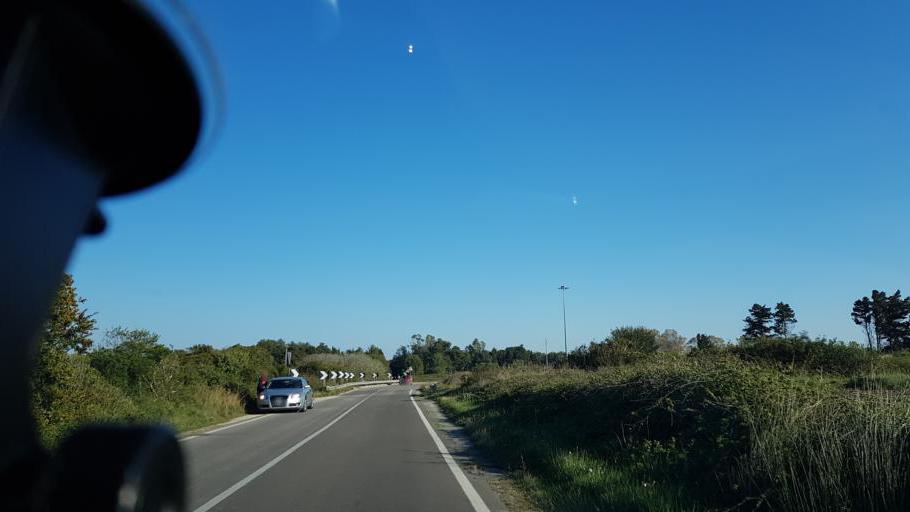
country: IT
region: Apulia
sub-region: Provincia di Lecce
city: Merine
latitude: 40.4107
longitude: 18.2568
